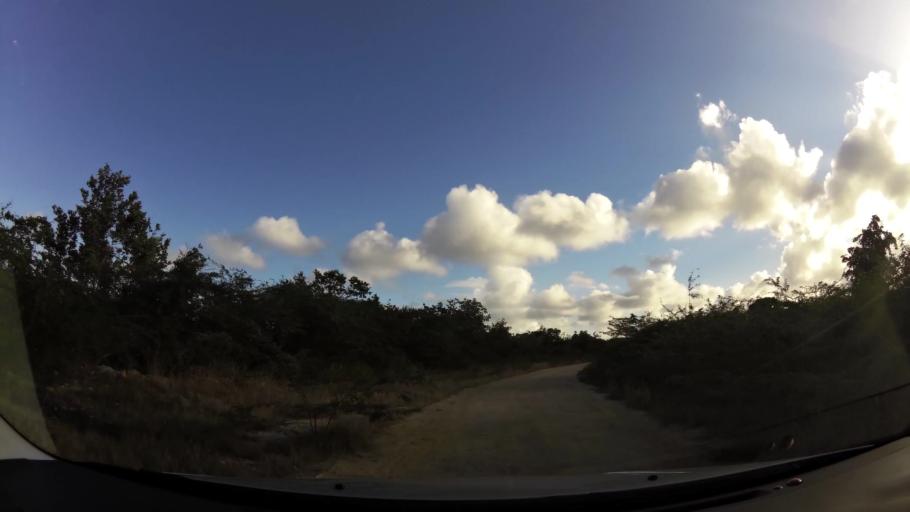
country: AG
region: Saint George
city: Piggotts
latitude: 17.1218
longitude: -61.7877
